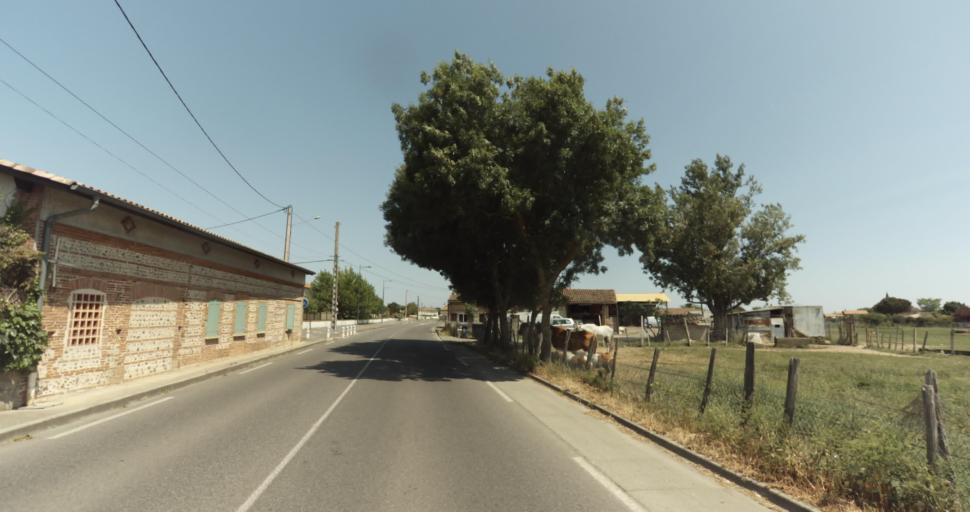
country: FR
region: Midi-Pyrenees
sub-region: Departement de la Haute-Garonne
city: La Salvetat-Saint-Gilles
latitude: 43.5639
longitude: 1.2656
